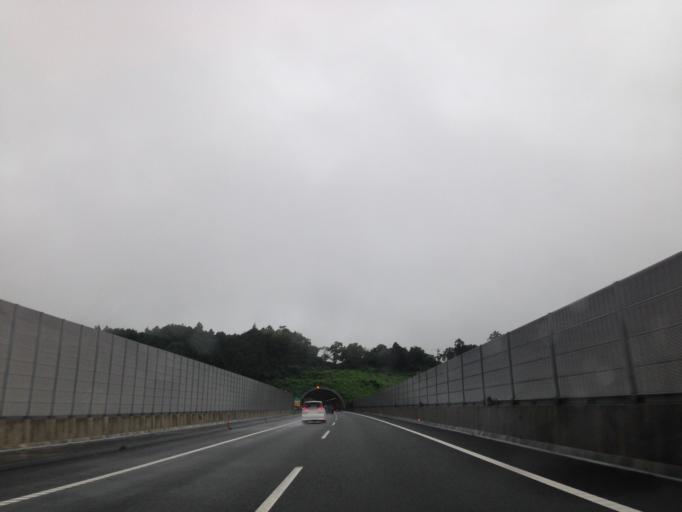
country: JP
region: Shizuoka
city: Mishima
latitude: 35.1925
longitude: 138.8890
